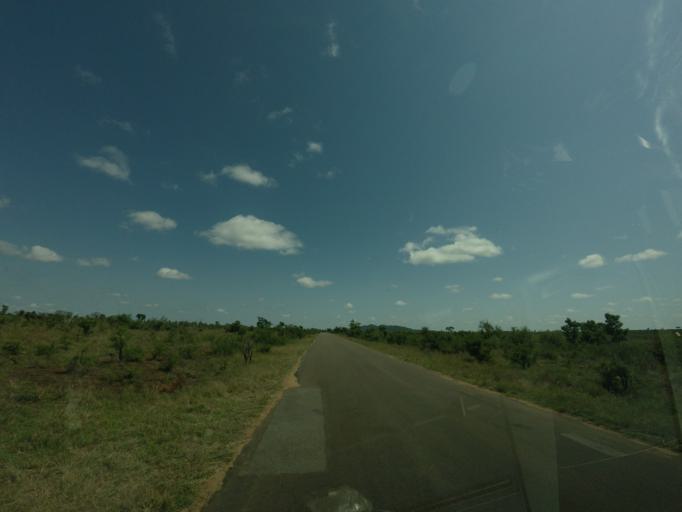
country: ZA
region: Mpumalanga
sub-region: Ehlanzeni District
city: Komatipoort
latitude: -25.0774
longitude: 31.9186
